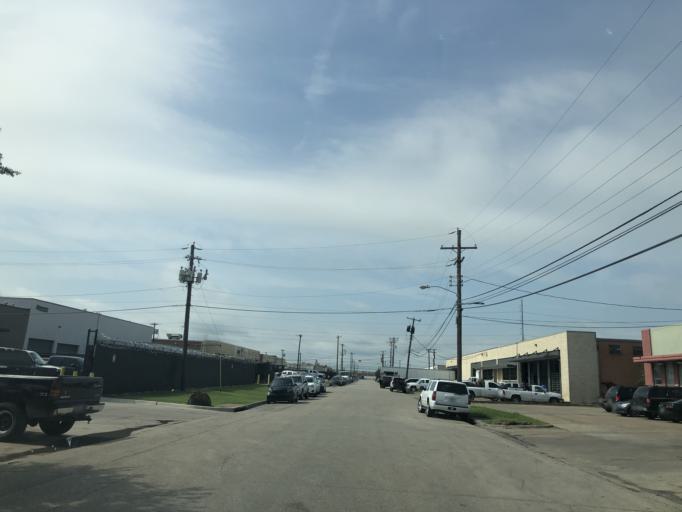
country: US
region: Texas
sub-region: Dallas County
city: Dallas
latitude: 32.8110
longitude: -96.8716
